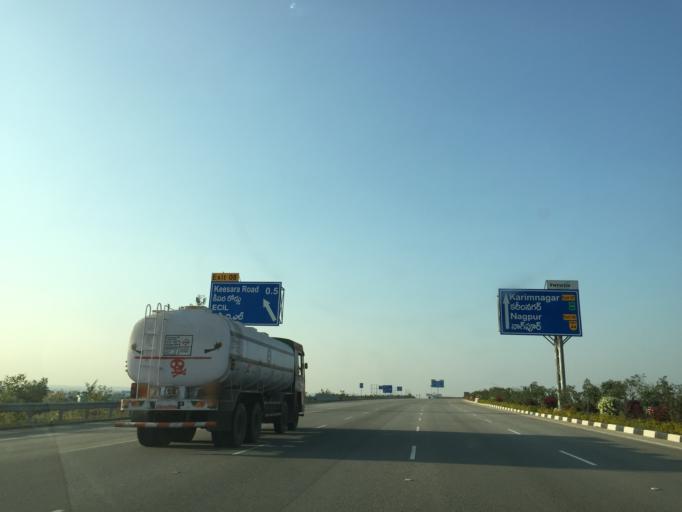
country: IN
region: Telangana
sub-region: Rangareddi
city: Ghatkesar
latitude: 17.5101
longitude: 78.6509
